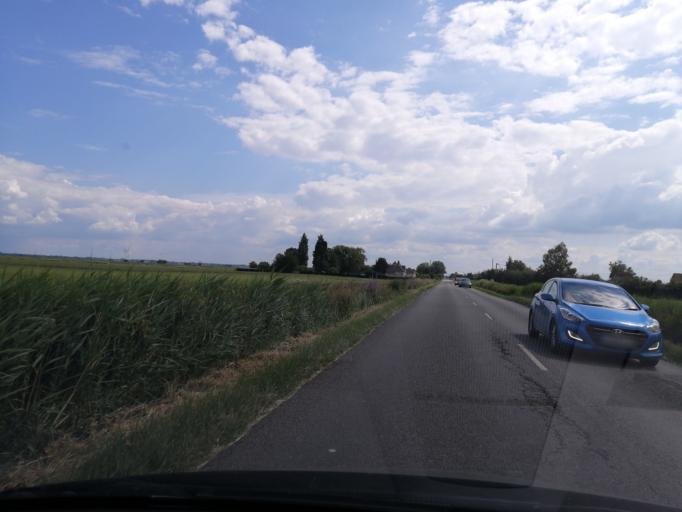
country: GB
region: England
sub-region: Cambridgeshire
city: Whittlesey
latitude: 52.5022
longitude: -0.1456
